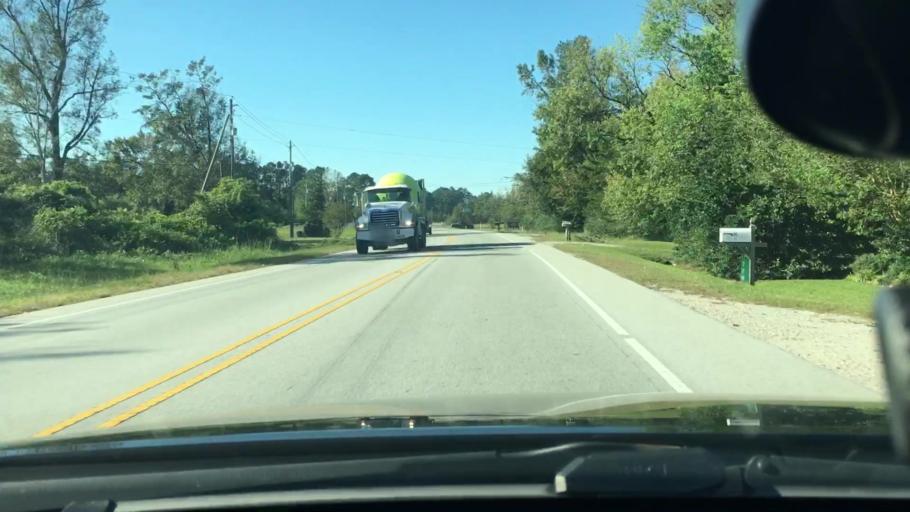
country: US
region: North Carolina
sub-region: Craven County
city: Trent Woods
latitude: 35.1575
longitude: -77.1144
